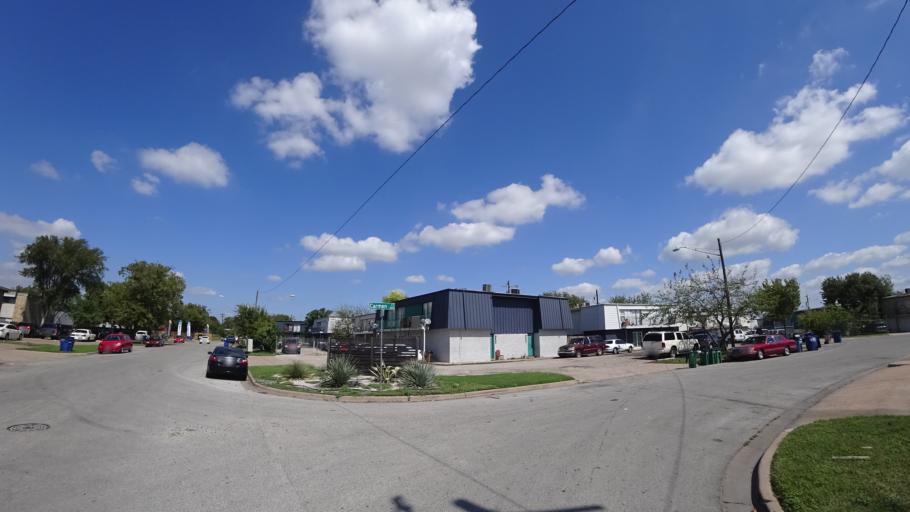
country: US
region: Texas
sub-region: Travis County
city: Austin
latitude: 30.3353
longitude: -97.7077
